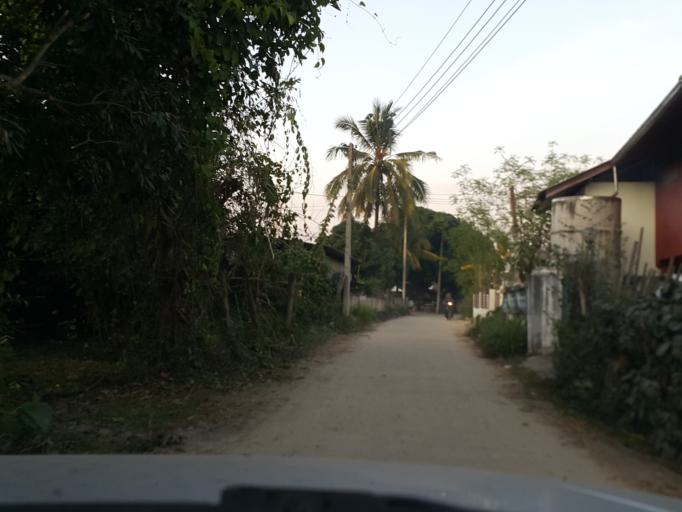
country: TH
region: Lamphun
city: Ban Thi
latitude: 18.5987
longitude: 99.2715
